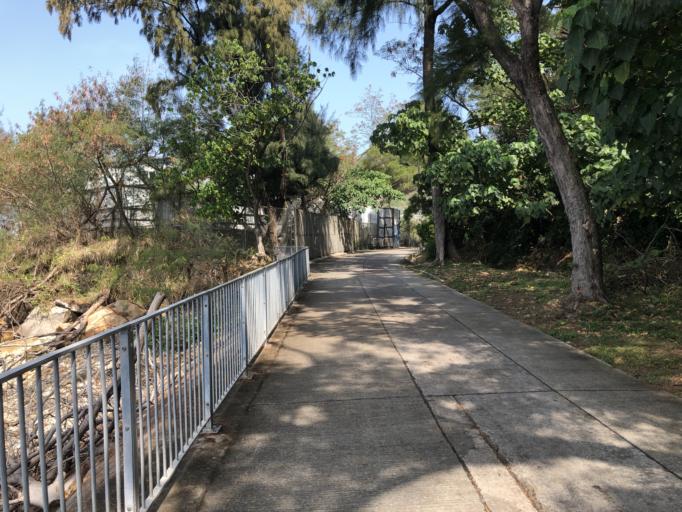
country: HK
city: Yung Shue Wan
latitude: 22.2153
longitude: 114.0255
